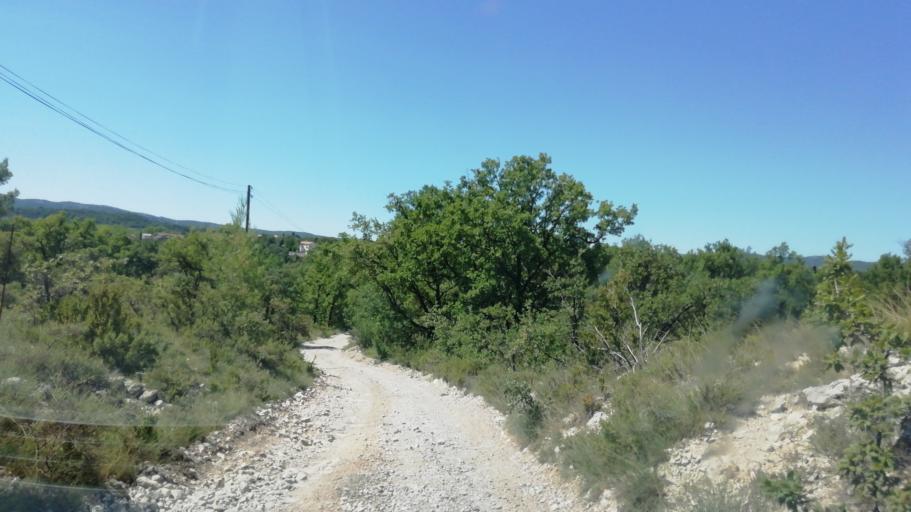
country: FR
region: Languedoc-Roussillon
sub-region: Departement de l'Herault
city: Saint-Martin-de-Londres
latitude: 43.8318
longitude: 3.7783
